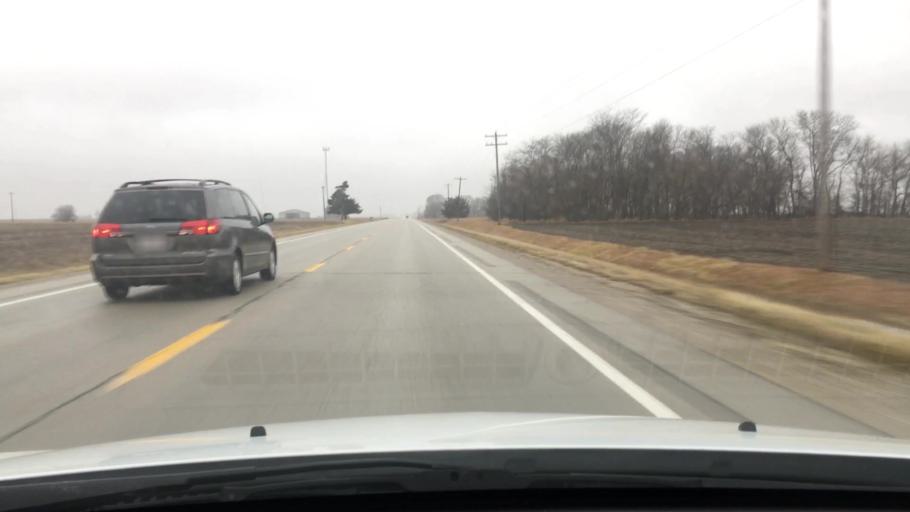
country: US
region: Illinois
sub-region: Livingston County
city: Flanagan
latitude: 40.8719
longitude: -88.8022
